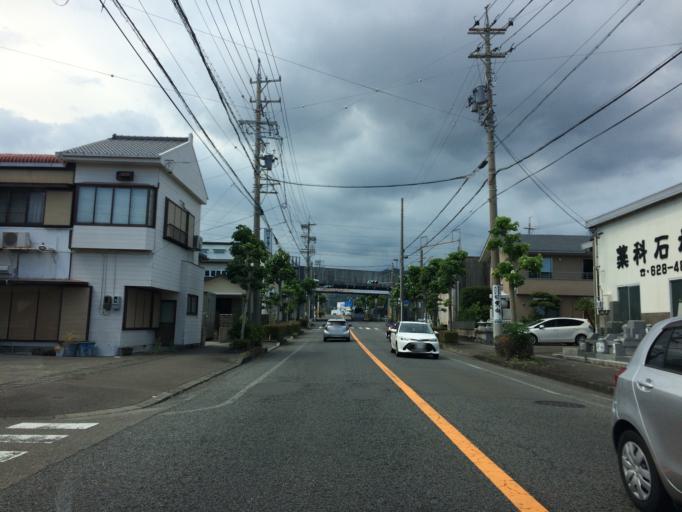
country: JP
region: Shizuoka
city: Yaizu
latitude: 34.8751
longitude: 138.3126
